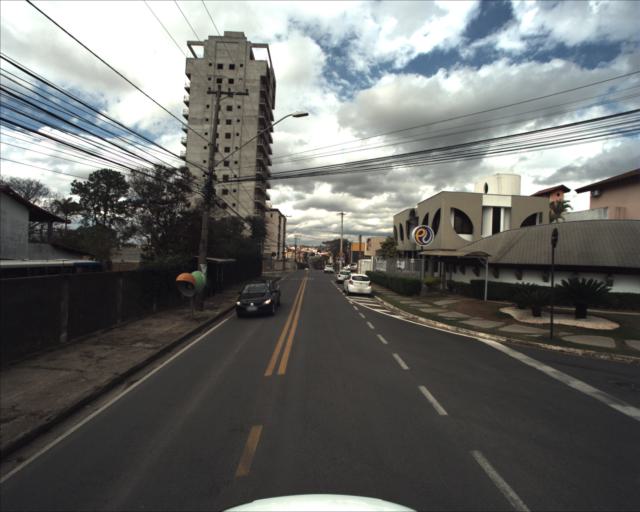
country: BR
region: Sao Paulo
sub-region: Sorocaba
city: Sorocaba
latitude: -23.5212
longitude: -47.4801
